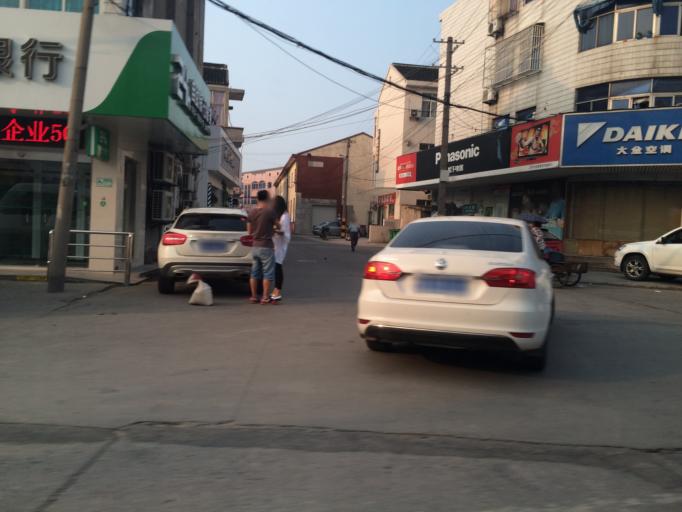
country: CN
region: Jiangsu Sheng
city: Xuxiake
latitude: 31.8125
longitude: 120.3008
